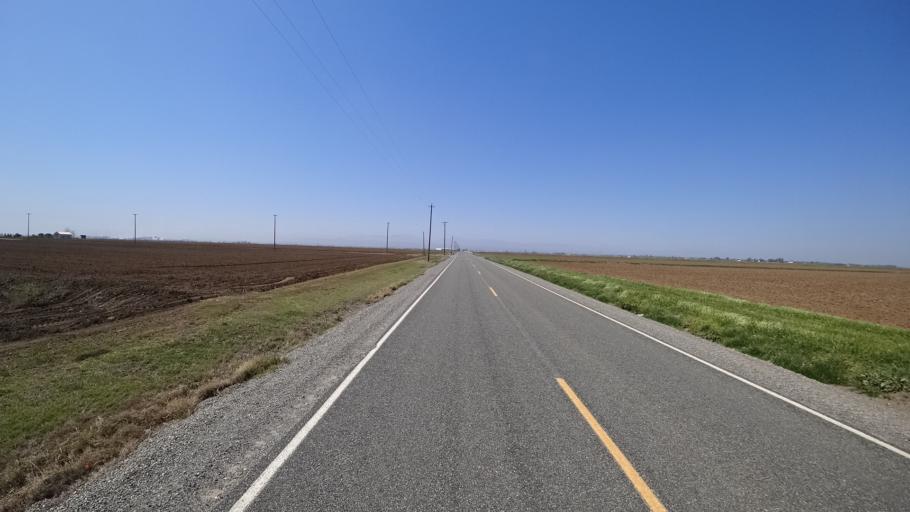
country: US
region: California
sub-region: Glenn County
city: Willows
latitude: 39.4947
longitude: -122.1541
